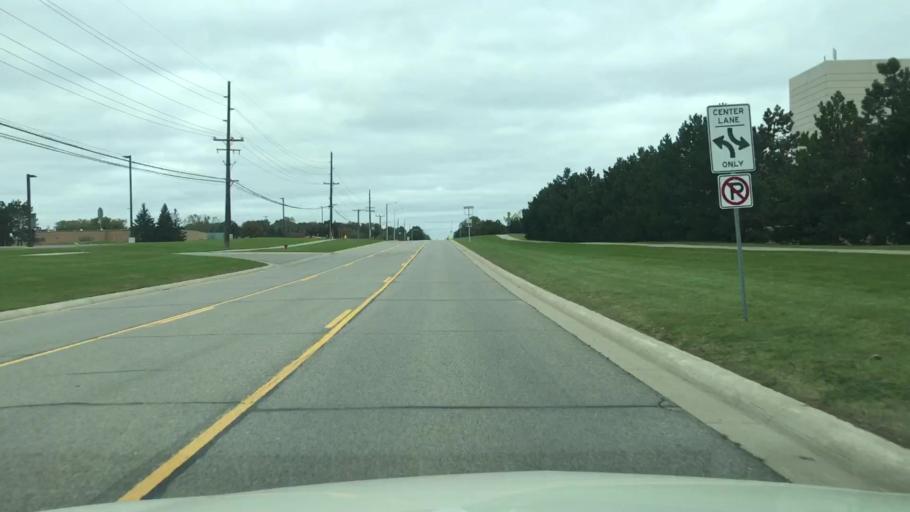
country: US
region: Michigan
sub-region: Oakland County
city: Rochester
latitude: 42.6980
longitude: -83.1235
